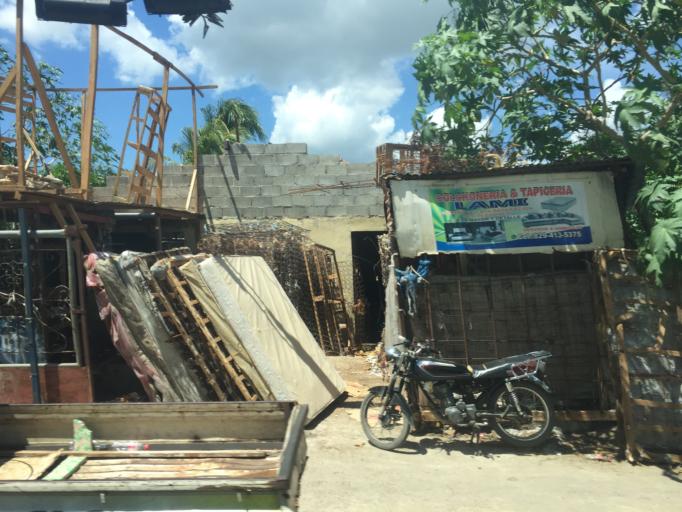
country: DO
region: Santiago
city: Santiago de los Caballeros
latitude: 19.4517
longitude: -70.7582
